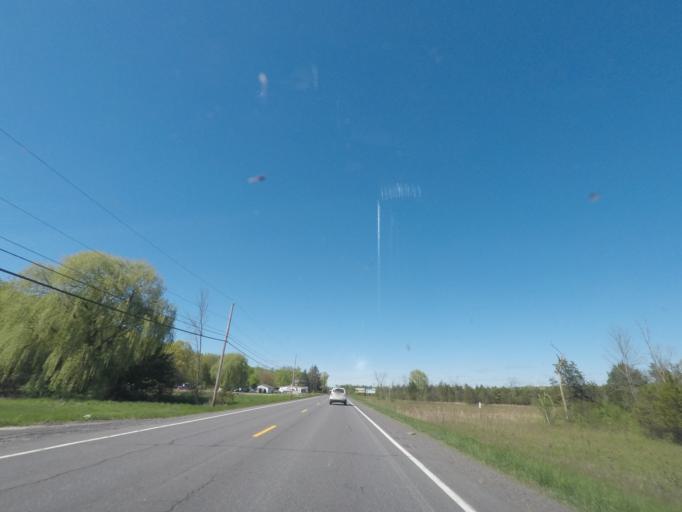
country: US
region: New York
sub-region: Greene County
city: Jefferson Heights
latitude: 42.2751
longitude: -73.8572
